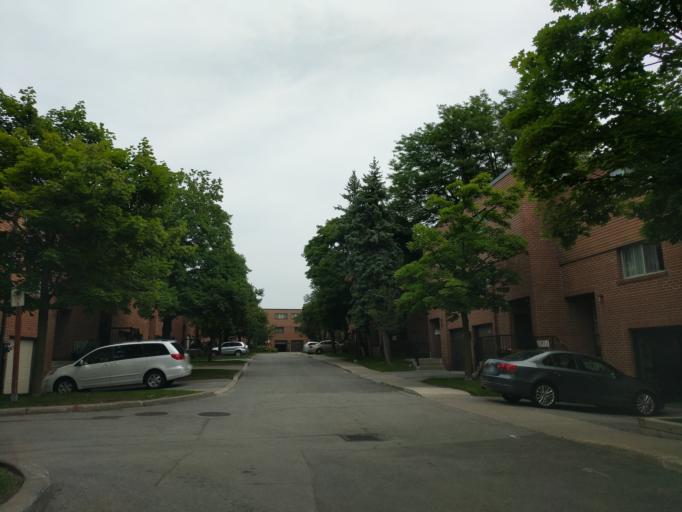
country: CA
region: Ontario
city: Willowdale
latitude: 43.8112
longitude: -79.3546
